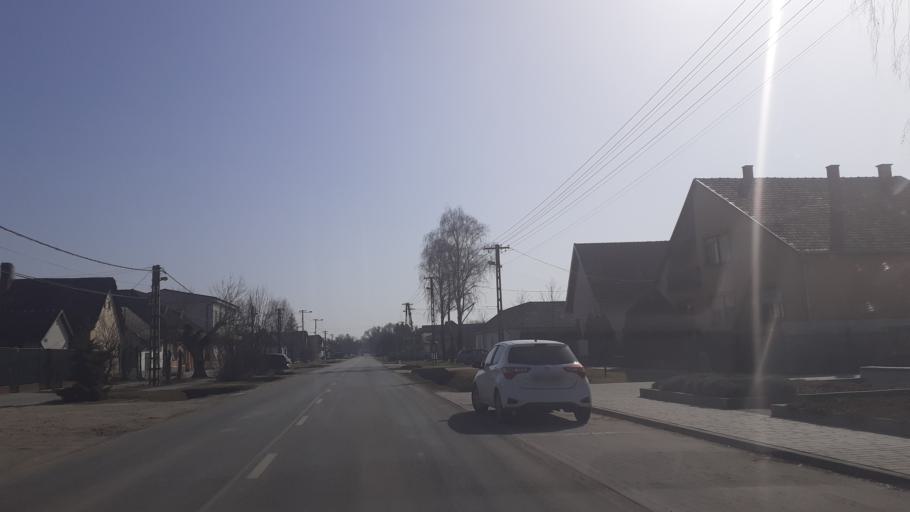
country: HU
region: Pest
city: Dabas
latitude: 47.1717
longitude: 19.3223
